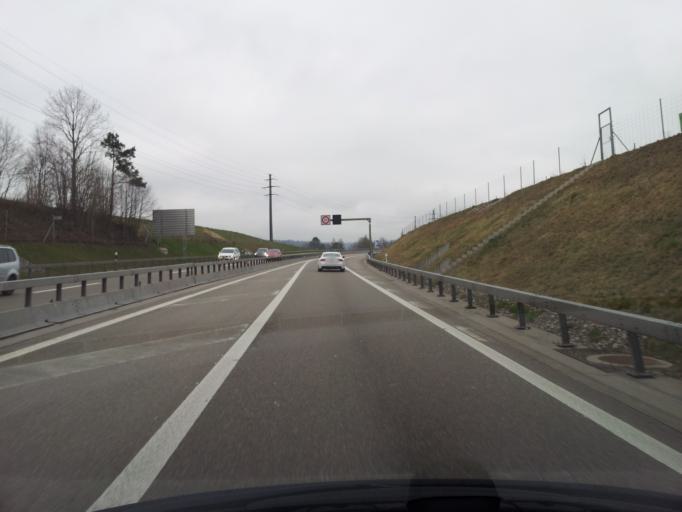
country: CH
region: Zurich
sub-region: Bezirk Andelfingen
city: Dachsen
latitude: 47.6692
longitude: 8.6237
